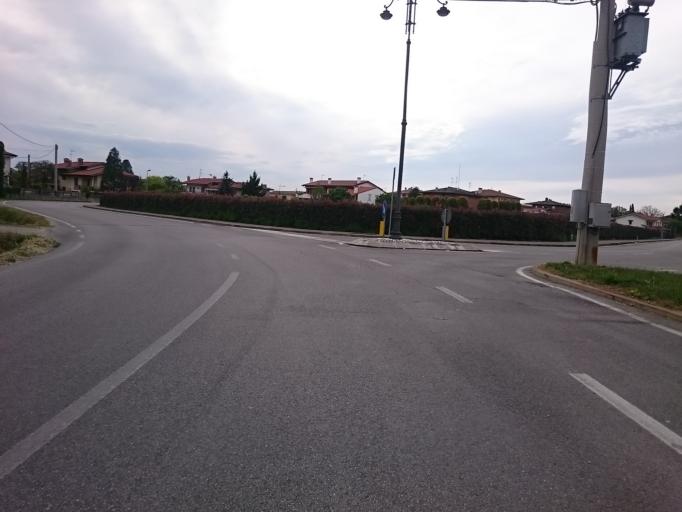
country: IT
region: Veneto
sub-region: Provincia di Padova
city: Sant'Elena
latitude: 45.1816
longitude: 11.7157
